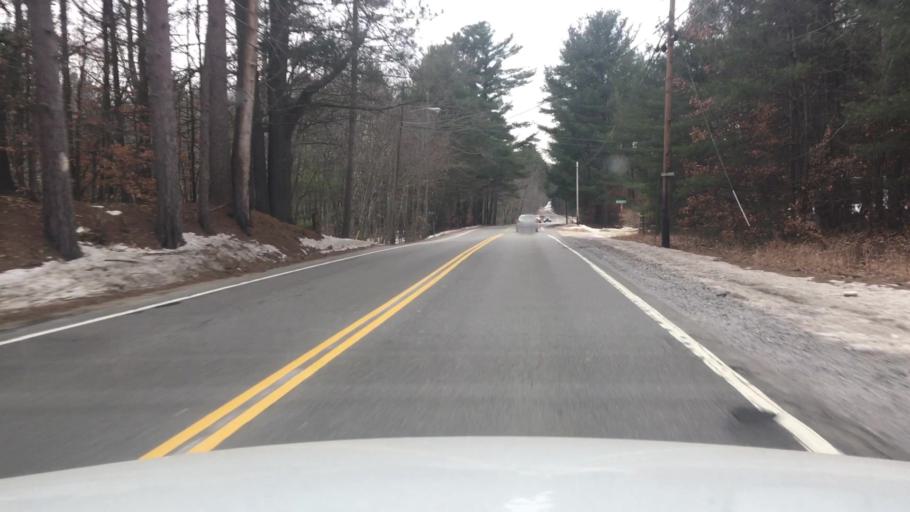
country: US
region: New Hampshire
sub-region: Merrimack County
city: Hopkinton
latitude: 43.1535
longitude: -71.6141
